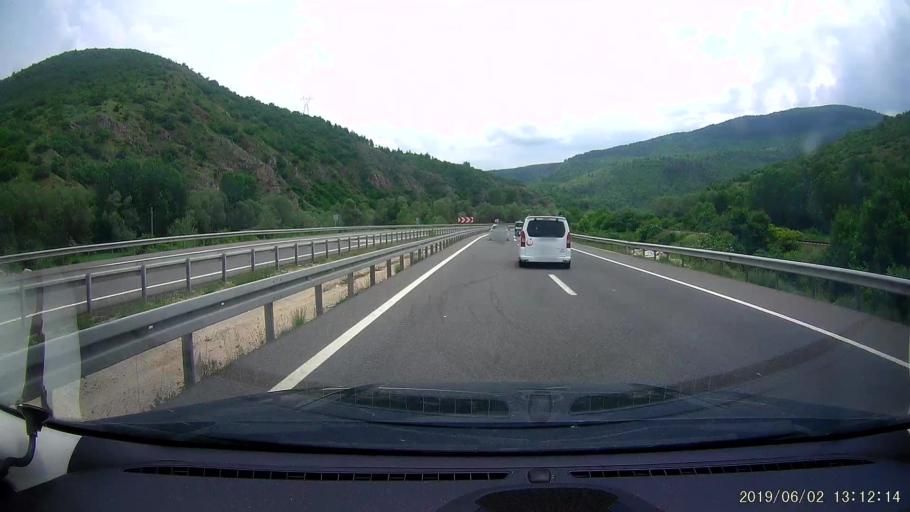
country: TR
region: Karabuk
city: Gozyeri
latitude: 40.8625
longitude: 32.6359
